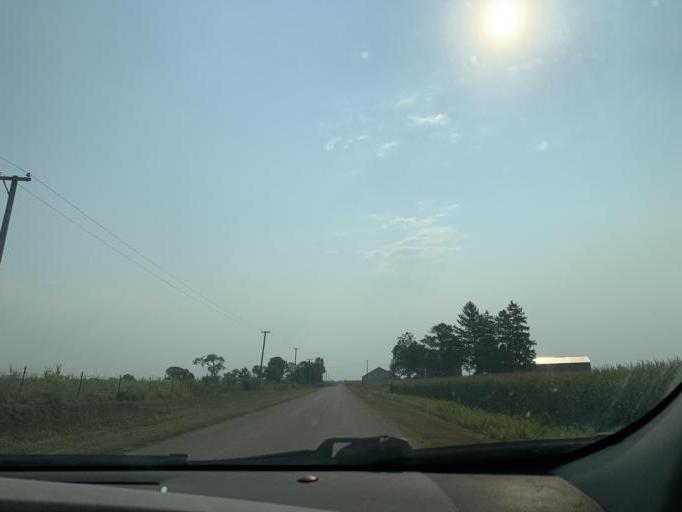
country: US
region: Illinois
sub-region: Whiteside County
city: Morrison
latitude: 41.8697
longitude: -89.9087
